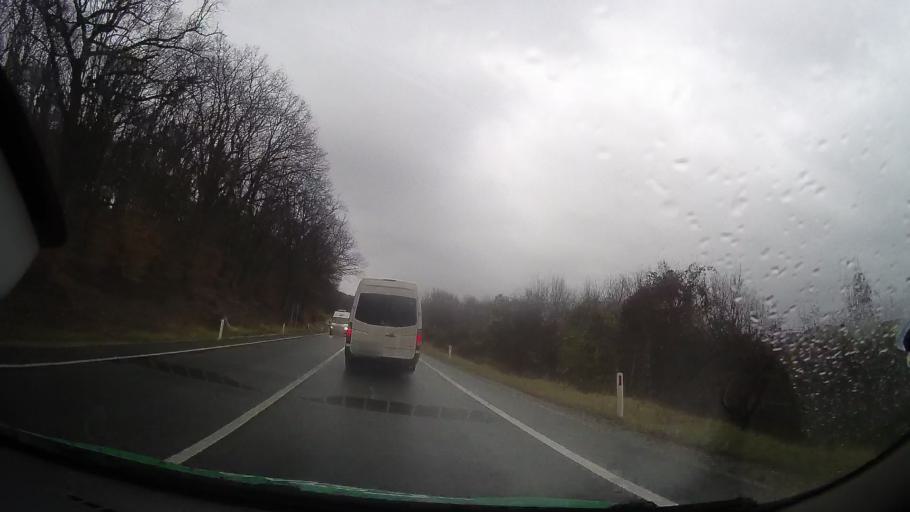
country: RO
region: Bistrita-Nasaud
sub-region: Comuna Sieu-Magherus
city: Sieu-Magherus
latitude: 47.0401
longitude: 24.4202
